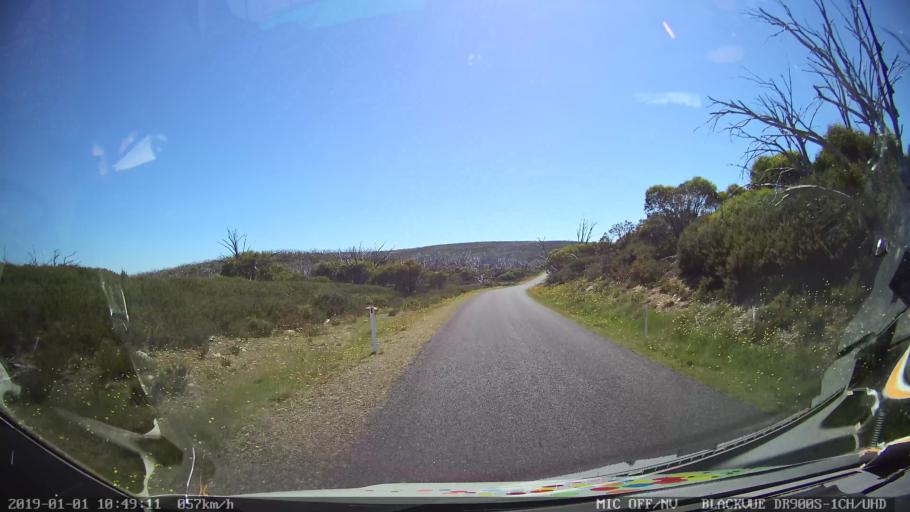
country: AU
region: New South Wales
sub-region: Snowy River
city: Jindabyne
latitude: -36.0357
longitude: 148.3677
